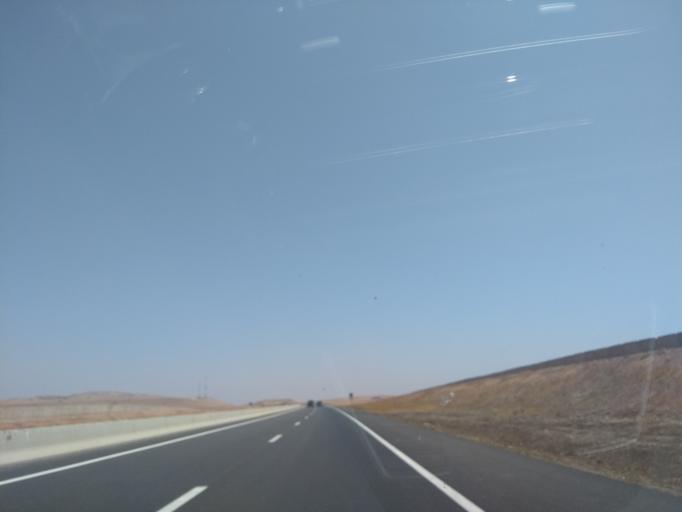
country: MA
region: Marrakech-Tensift-Al Haouz
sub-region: Kelaa-Des-Sraghna
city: Sidi Abdallah
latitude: 32.2978
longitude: -7.9601
